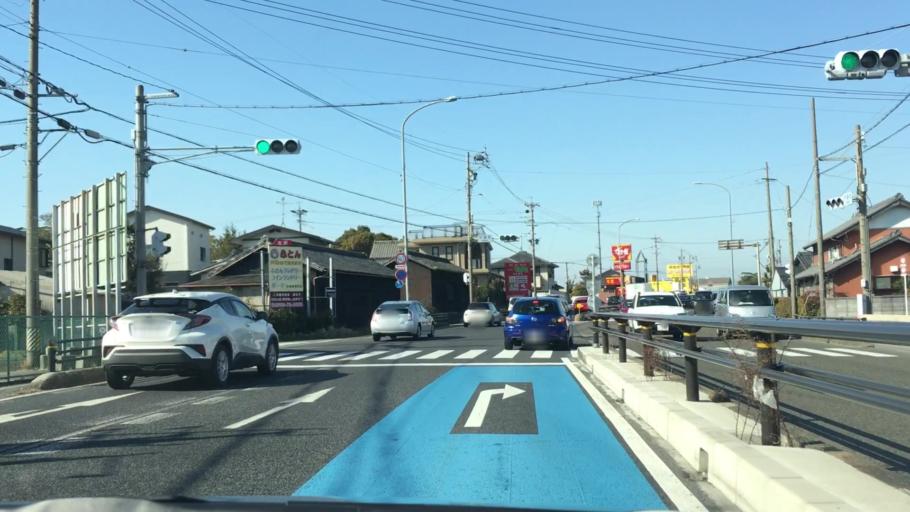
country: JP
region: Aichi
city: Anjo
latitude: 34.9725
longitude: 137.1209
